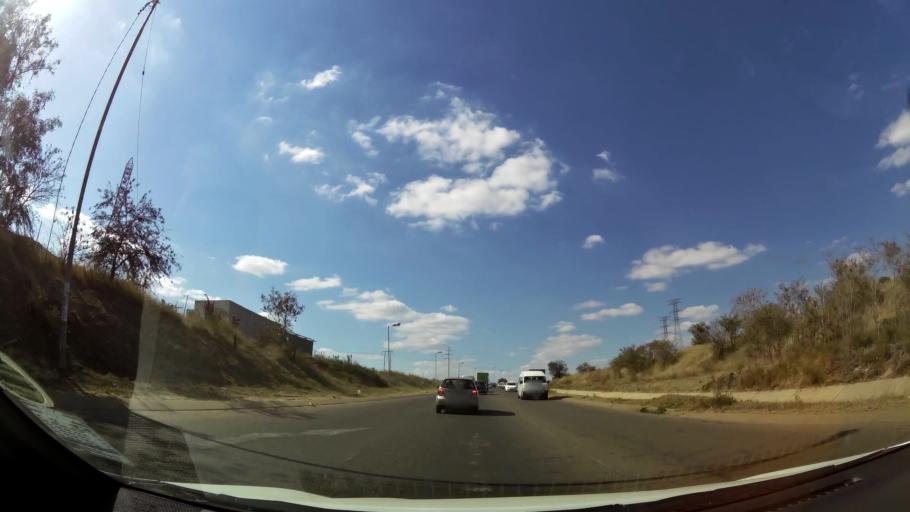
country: ZA
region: Gauteng
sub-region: City of Tshwane Metropolitan Municipality
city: Cullinan
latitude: -25.7408
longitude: 28.3792
